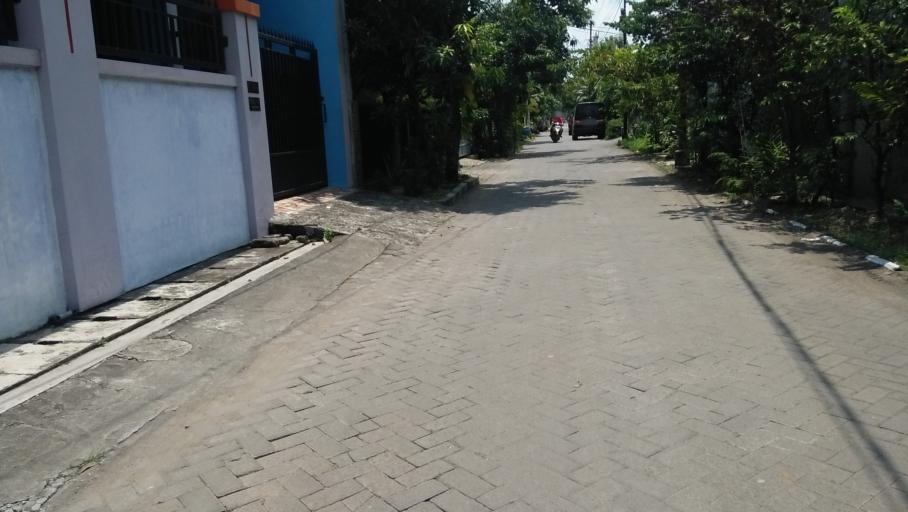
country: ID
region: Central Java
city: Mranggen
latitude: -7.0285
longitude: 110.4622
